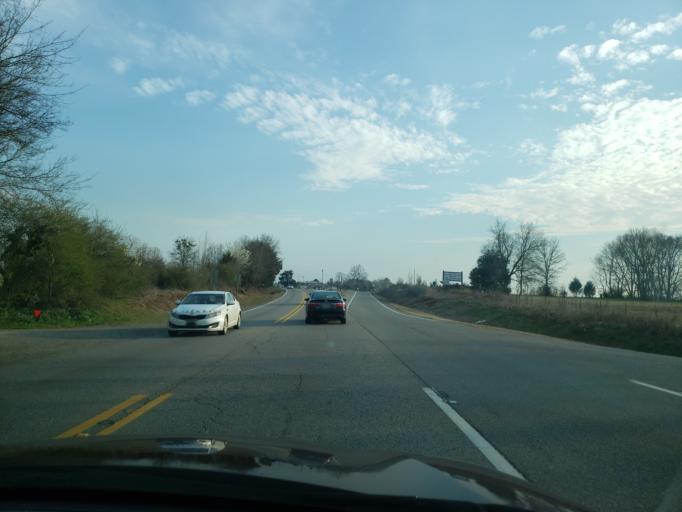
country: US
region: Alabama
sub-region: Hale County
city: Moundville
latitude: 32.9159
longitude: -87.6398
